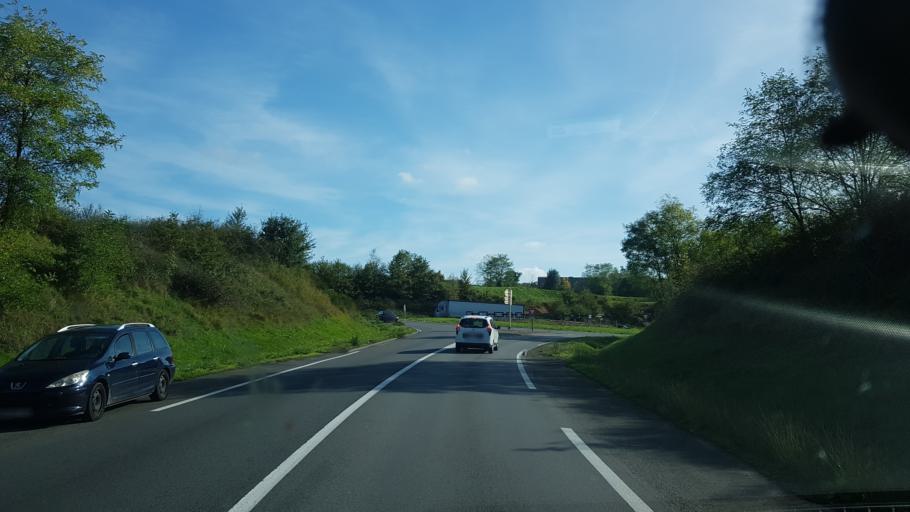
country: FR
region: Poitou-Charentes
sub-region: Departement de la Charente
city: Chasseneuil-sur-Bonnieure
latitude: 45.8330
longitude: 0.4685
